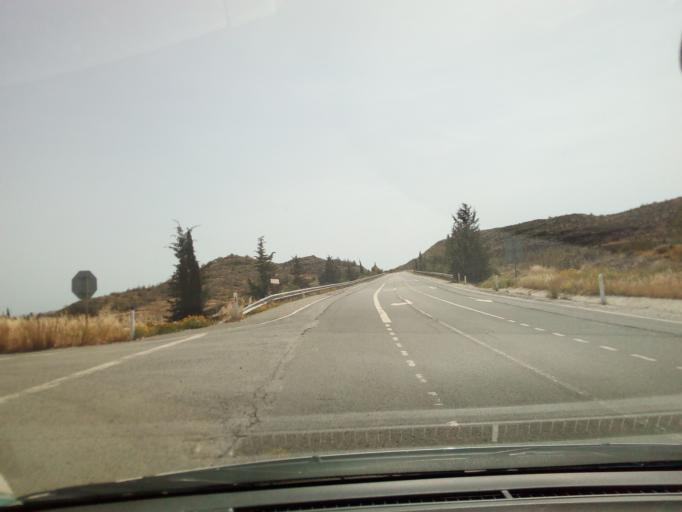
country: CY
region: Larnaka
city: Athienou
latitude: 35.0100
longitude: 33.5626
